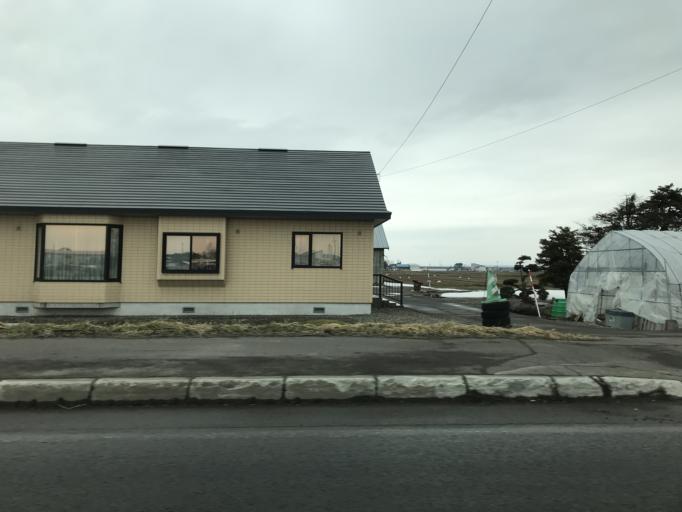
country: JP
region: Hokkaido
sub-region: Asahikawa-shi
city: Asahikawa
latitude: 43.8282
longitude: 142.4207
